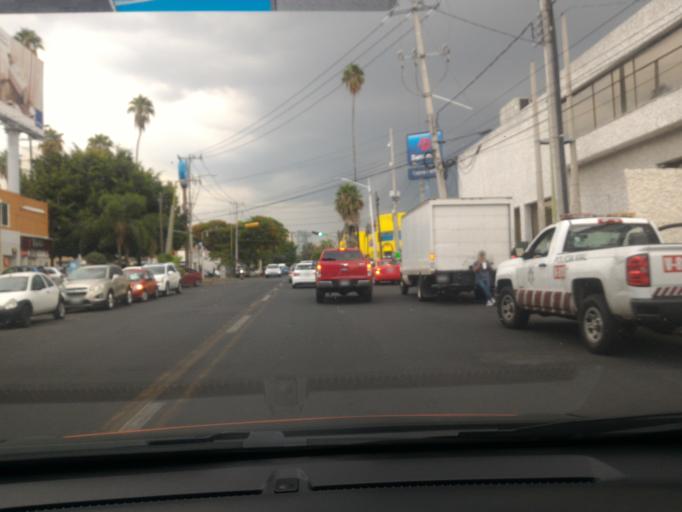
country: MX
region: Jalisco
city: Guadalajara
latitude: 20.6641
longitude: -103.3591
